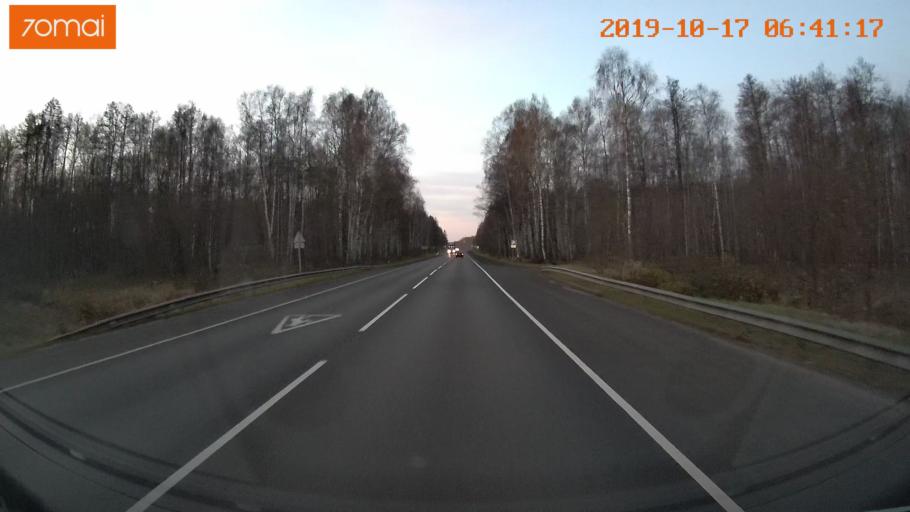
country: RU
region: Ivanovo
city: Nerl'
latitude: 56.6170
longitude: 40.5616
